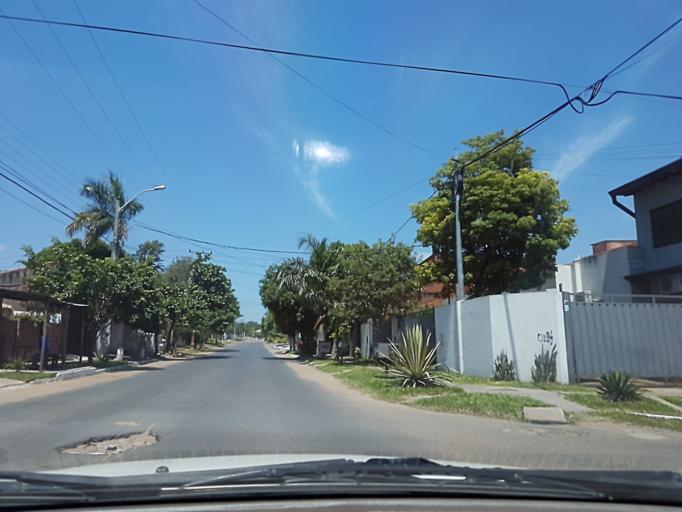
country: PY
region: Central
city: Fernando de la Mora
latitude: -25.3015
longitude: -57.5430
